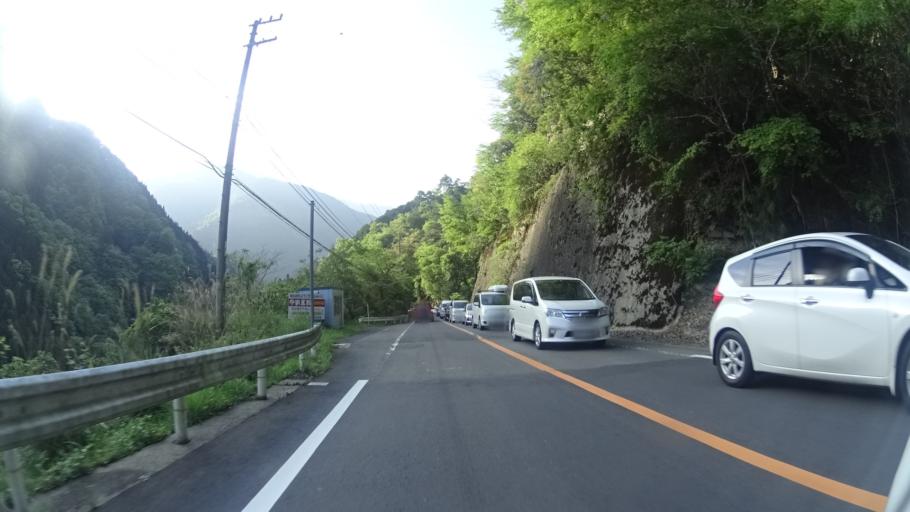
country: JP
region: Tokushima
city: Ikedacho
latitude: 33.8862
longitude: 133.8202
